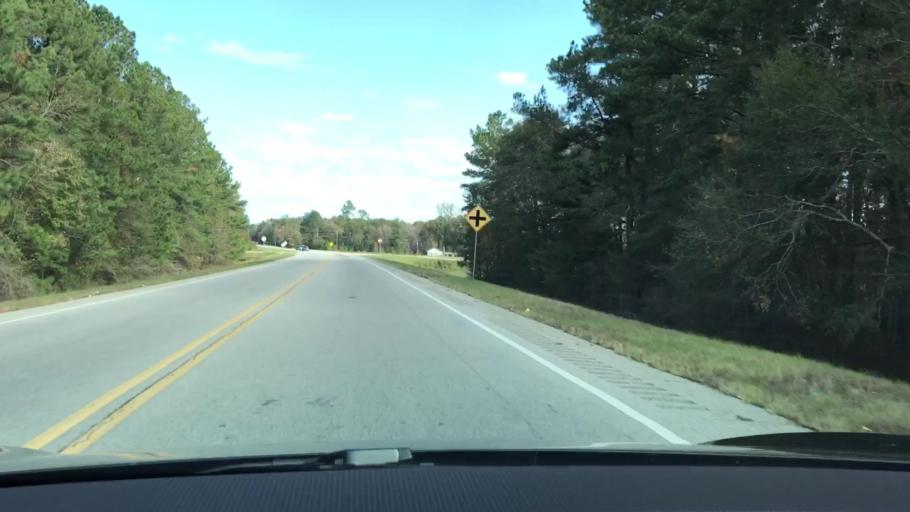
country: US
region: Georgia
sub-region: Jefferson County
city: Louisville
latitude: 32.9611
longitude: -82.3911
